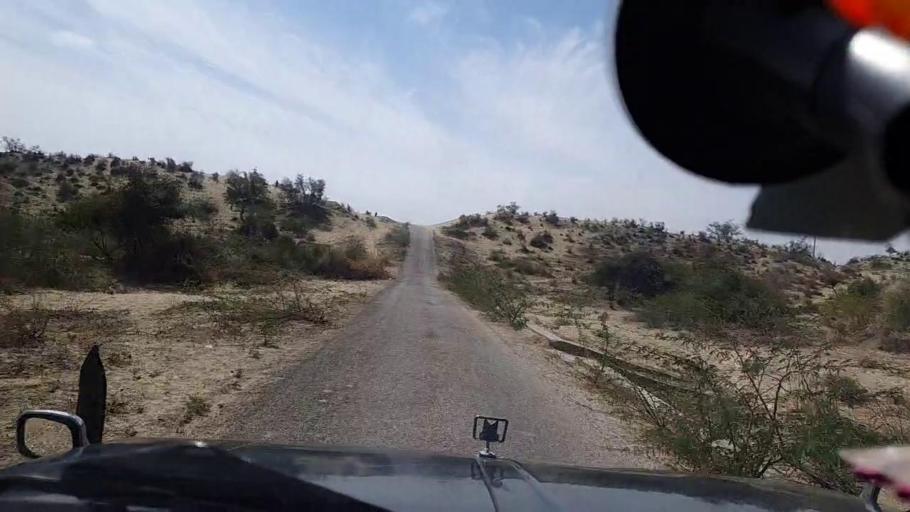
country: PK
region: Sindh
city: Diplo
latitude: 24.4151
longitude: 69.5851
